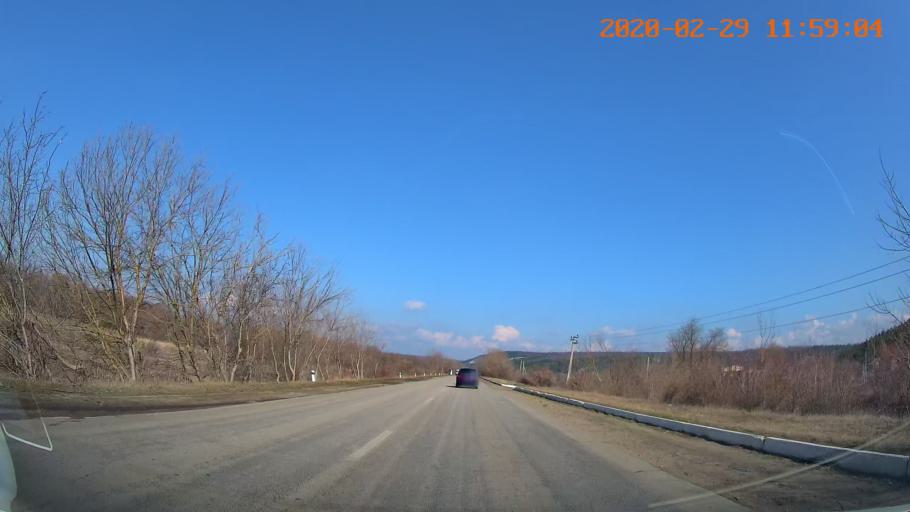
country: MD
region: Telenesti
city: Ribnita
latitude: 47.8209
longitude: 29.0148
